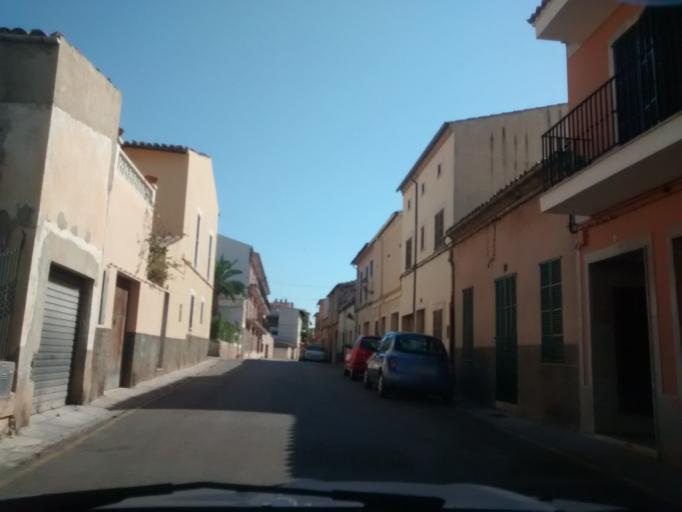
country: ES
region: Balearic Islands
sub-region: Illes Balears
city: Alaro
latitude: 39.7035
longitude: 2.7902
